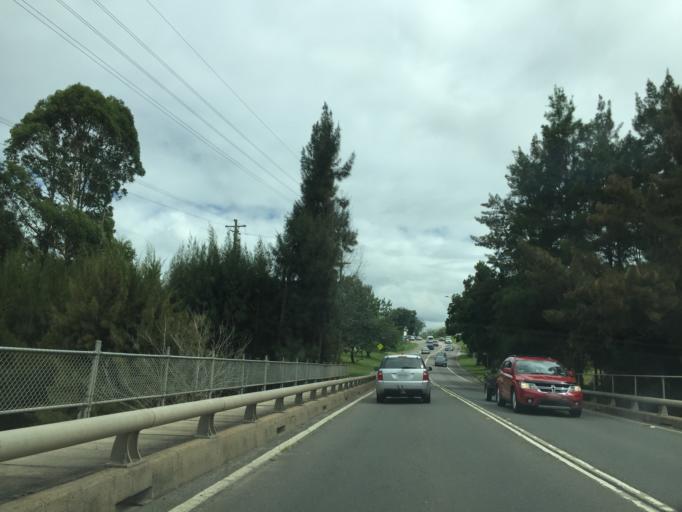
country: AU
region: New South Wales
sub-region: Hawkesbury
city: Richmond
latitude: -33.5846
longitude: 150.7239
